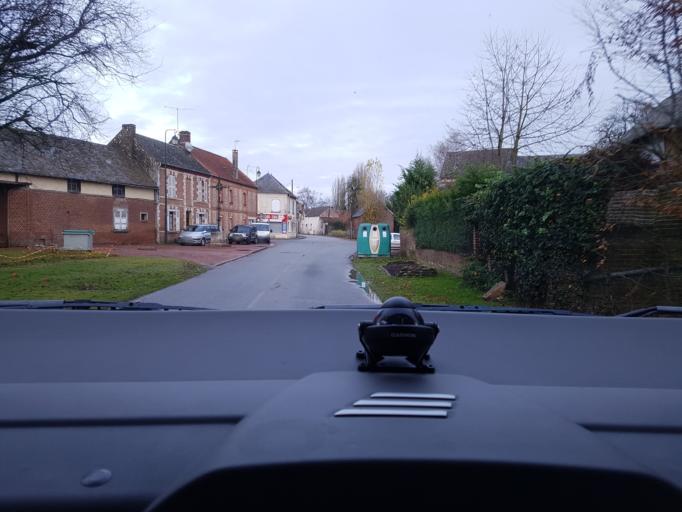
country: FR
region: Picardie
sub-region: Departement de l'Oise
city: Songeons
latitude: 49.5809
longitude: 1.8704
